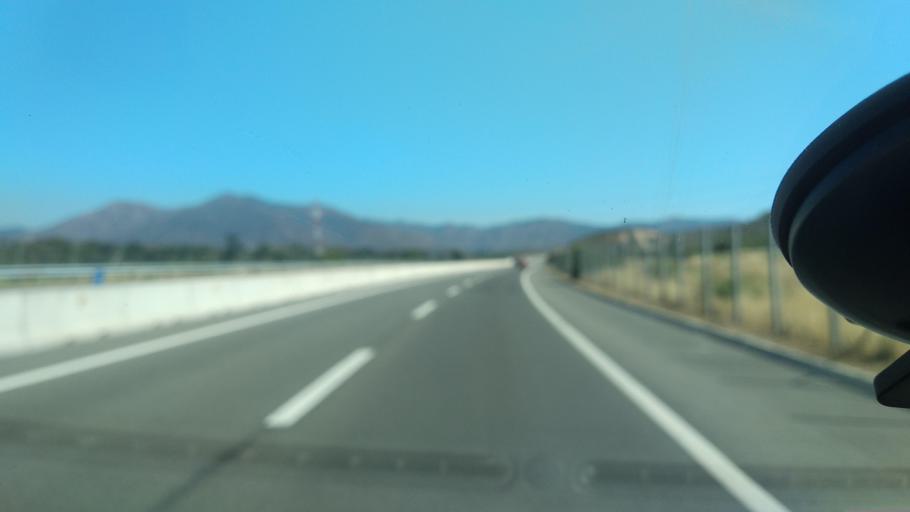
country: CL
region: Valparaiso
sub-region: Provincia de Marga Marga
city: Limache
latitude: -33.0171
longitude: -71.3199
